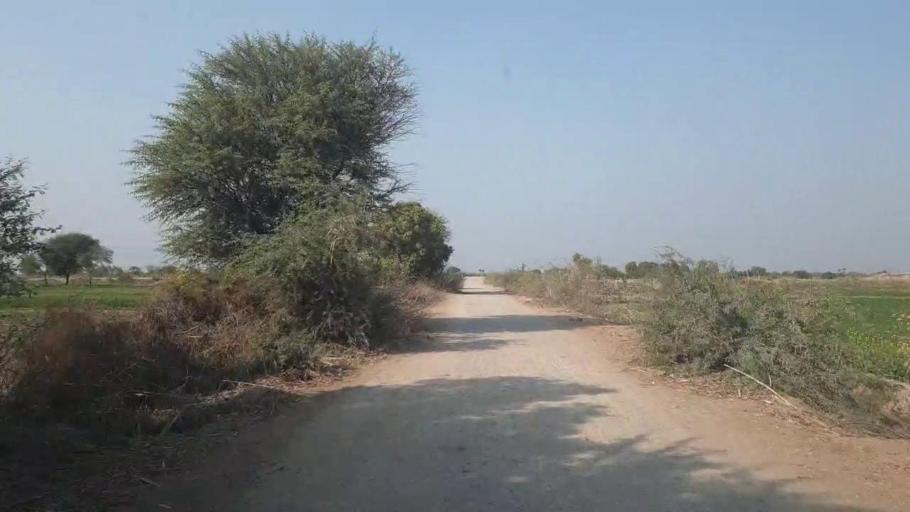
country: PK
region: Sindh
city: Tando Allahyar
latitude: 25.4434
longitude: 68.7873
